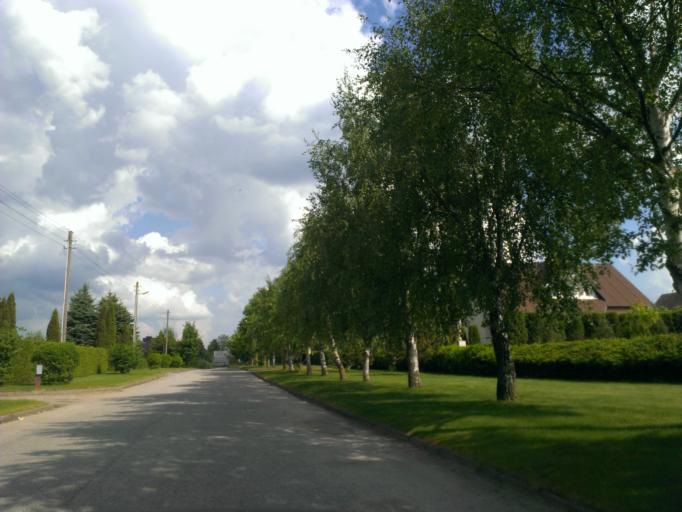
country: LT
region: Klaipedos apskritis
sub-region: Klaipeda
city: Palanga
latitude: 55.9057
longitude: 21.1320
